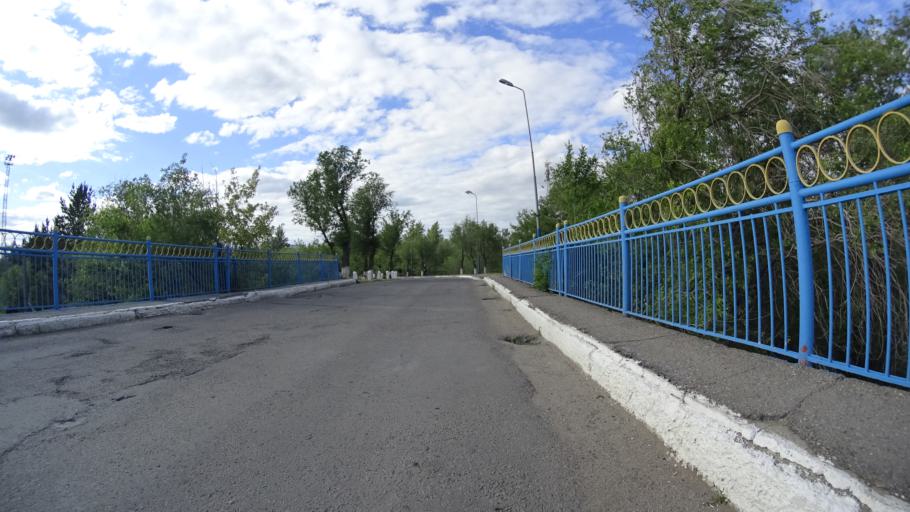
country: RU
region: Chelyabinsk
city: Troitsk
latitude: 54.0397
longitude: 61.6397
